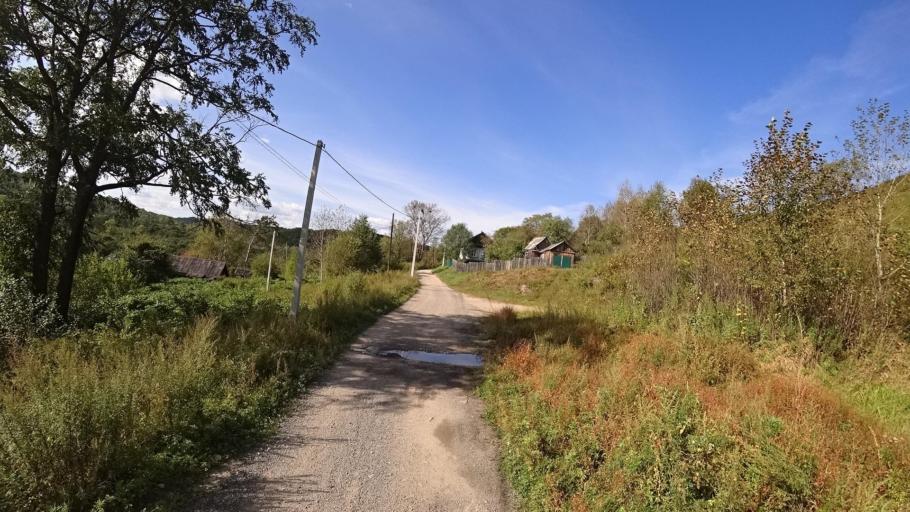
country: RU
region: Jewish Autonomous Oblast
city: Birakan
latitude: 49.0005
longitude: 131.7215
